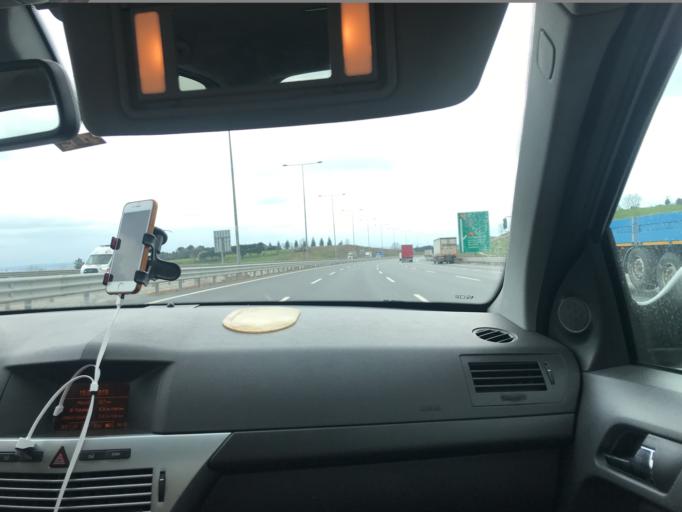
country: TR
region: Istanbul
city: Sultanbeyli
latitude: 40.9899
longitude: 29.3269
